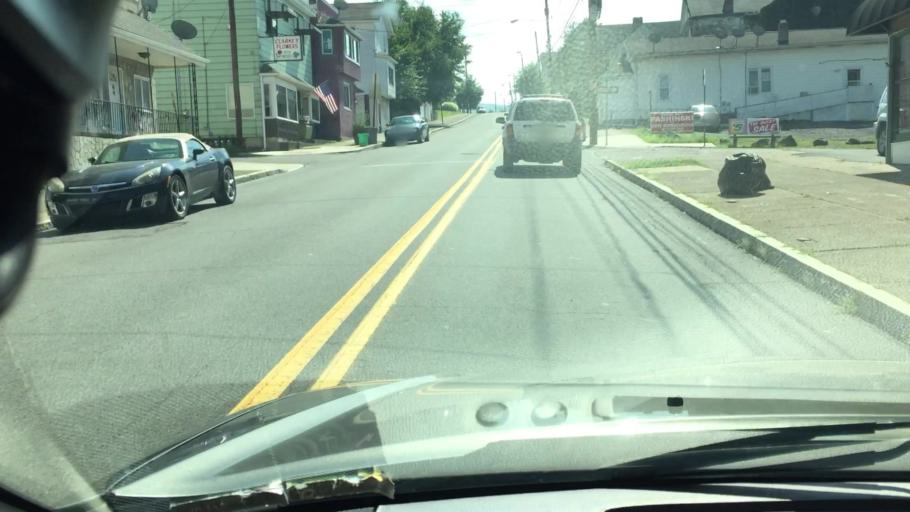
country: US
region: Pennsylvania
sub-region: Luzerne County
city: Ashley
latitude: 41.2161
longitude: -75.8979
